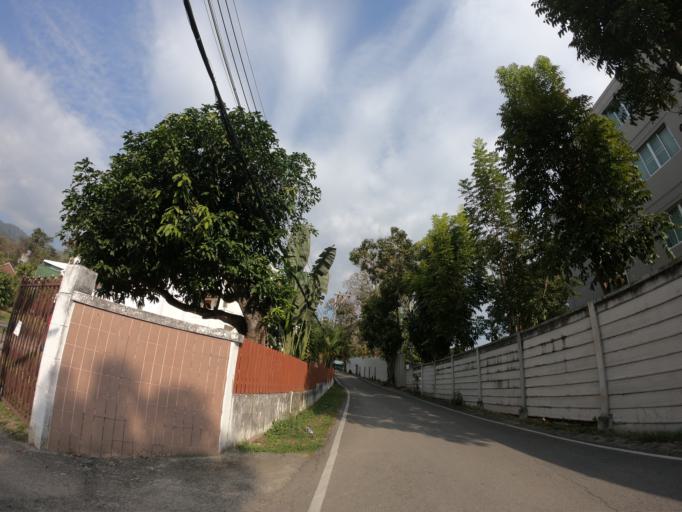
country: TH
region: Chiang Mai
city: Chiang Mai
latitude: 18.7925
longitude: 98.9485
